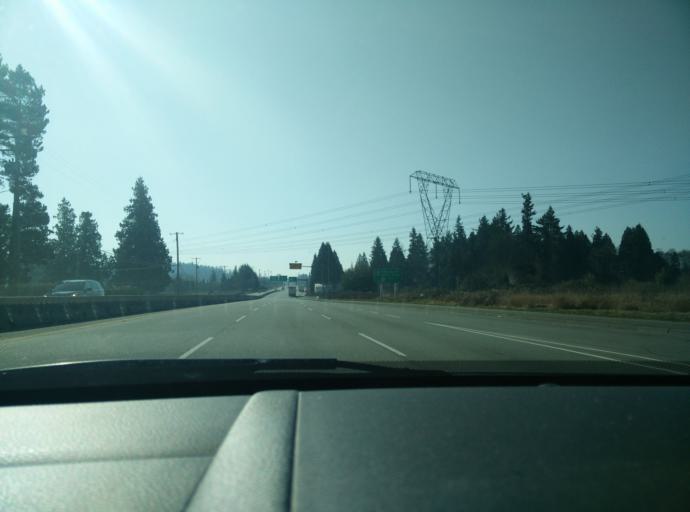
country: US
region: Washington
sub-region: Whatcom County
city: Blaine
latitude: 49.0138
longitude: -122.7354
